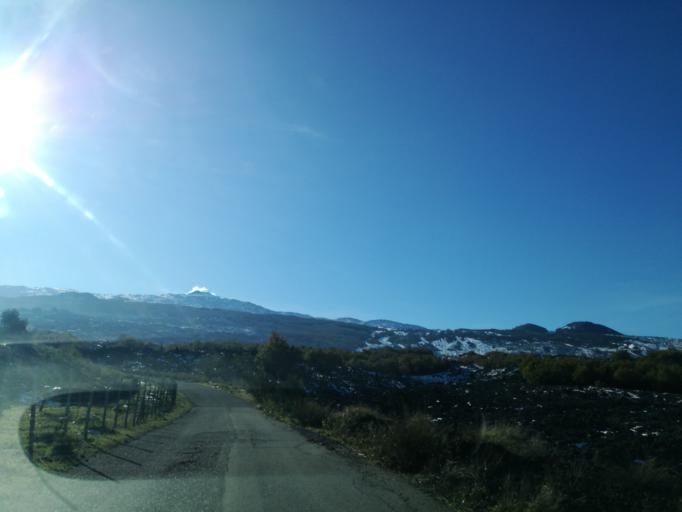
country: IT
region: Sicily
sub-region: Catania
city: Randazzo
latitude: 37.8621
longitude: 14.9794
